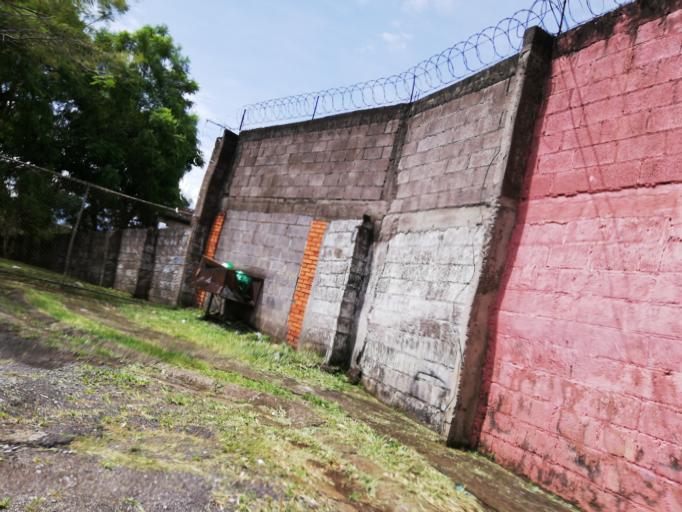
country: CR
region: Alajuela
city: Alajuela
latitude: 10.0177
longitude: -84.1950
